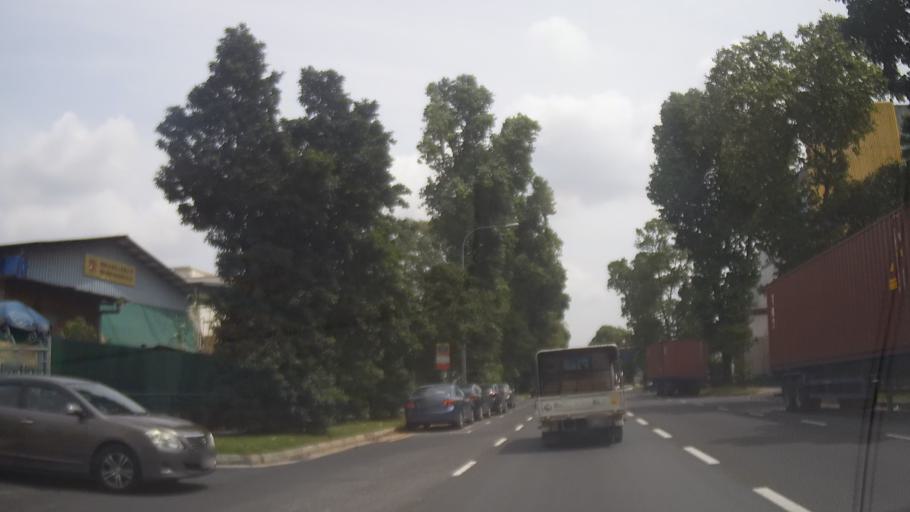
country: MY
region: Johor
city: Johor Bahru
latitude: 1.4165
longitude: 103.7463
